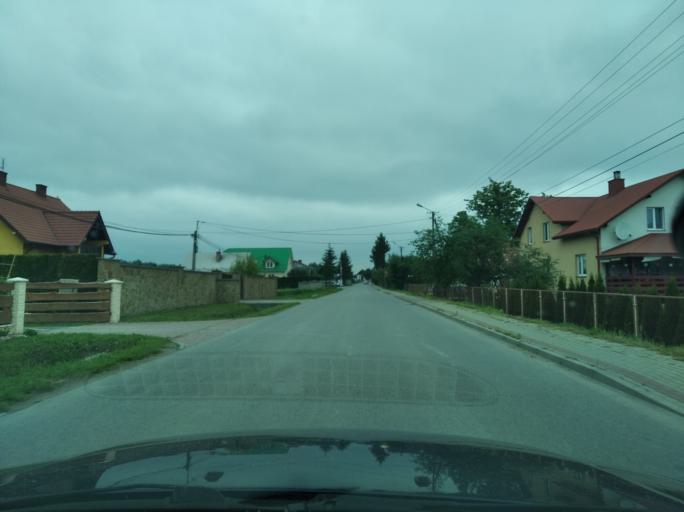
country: PL
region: Subcarpathian Voivodeship
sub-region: Powiat ropczycko-sedziszowski
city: Sedziszow Malopolski
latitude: 50.0968
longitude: 21.6648
